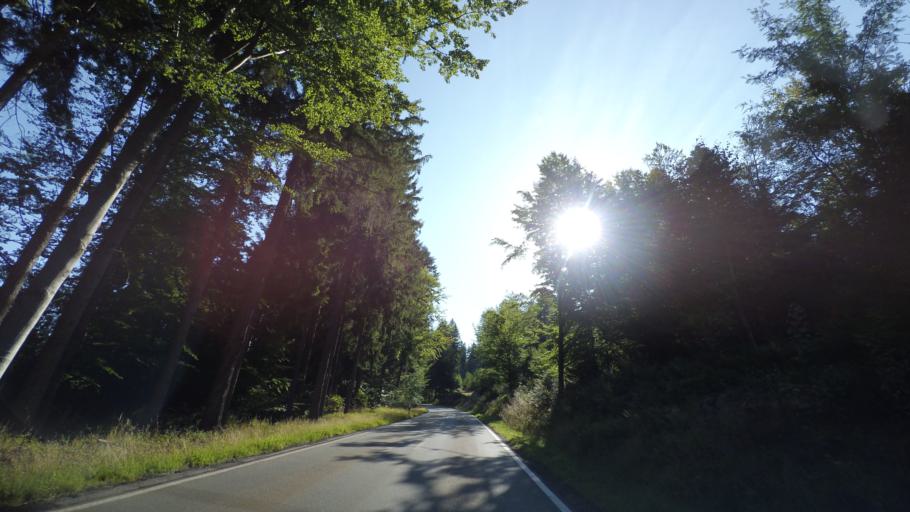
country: DE
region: Bavaria
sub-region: Upper Palatinate
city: Arrach
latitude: 49.1693
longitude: 12.9949
